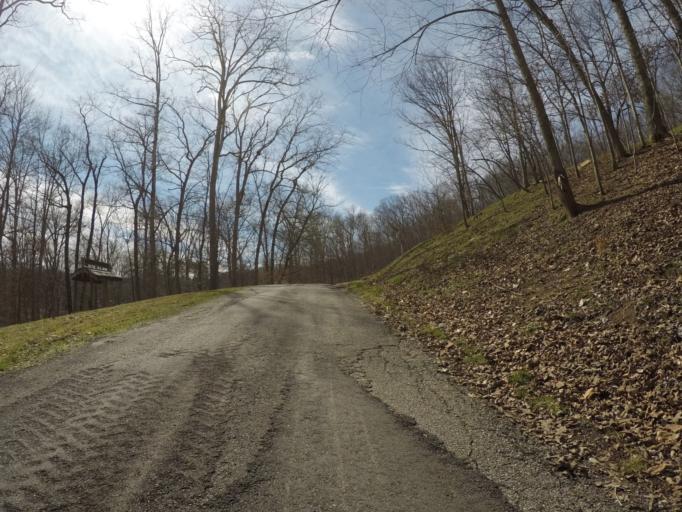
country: US
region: West Virginia
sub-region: Wayne County
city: Ceredo
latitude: 38.3637
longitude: -82.5338
